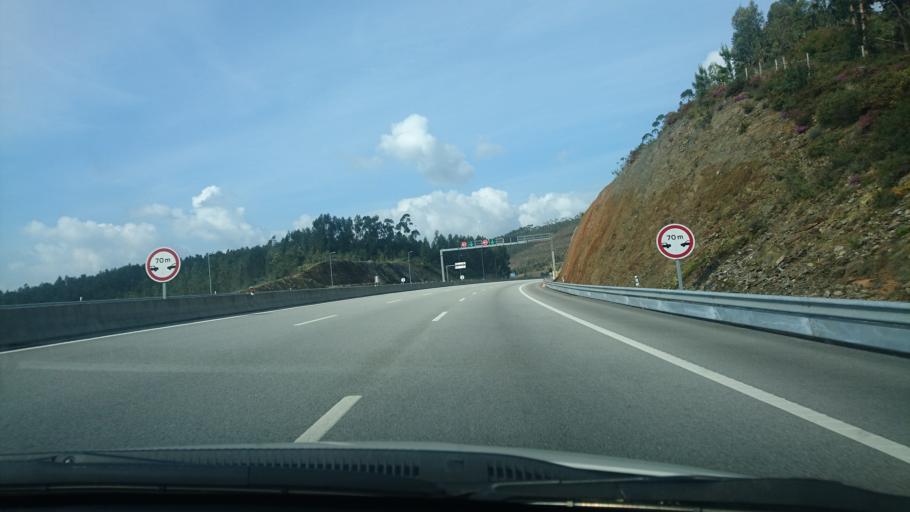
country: PT
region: Porto
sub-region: Gondomar
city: Foz do Sousa
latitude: 41.0985
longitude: -8.4567
